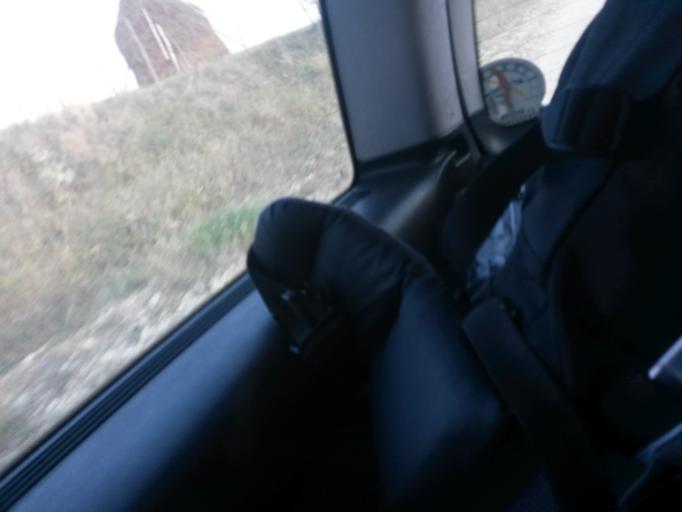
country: RO
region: Alba
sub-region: Comuna Livezile
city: Livezile
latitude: 46.3206
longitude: 23.5504
